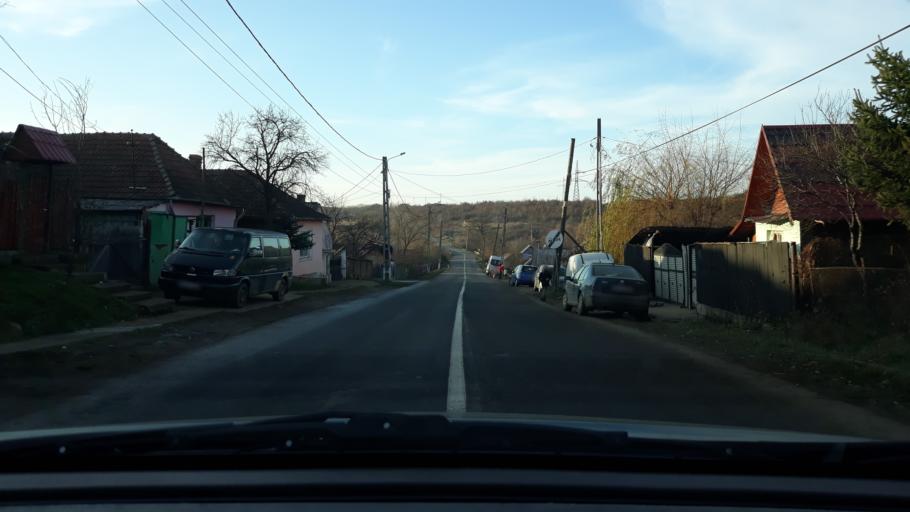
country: RO
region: Bihor
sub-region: Comuna Suplacu de Barcau
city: Suplacu de Barcau
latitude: 47.2635
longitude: 22.5154
